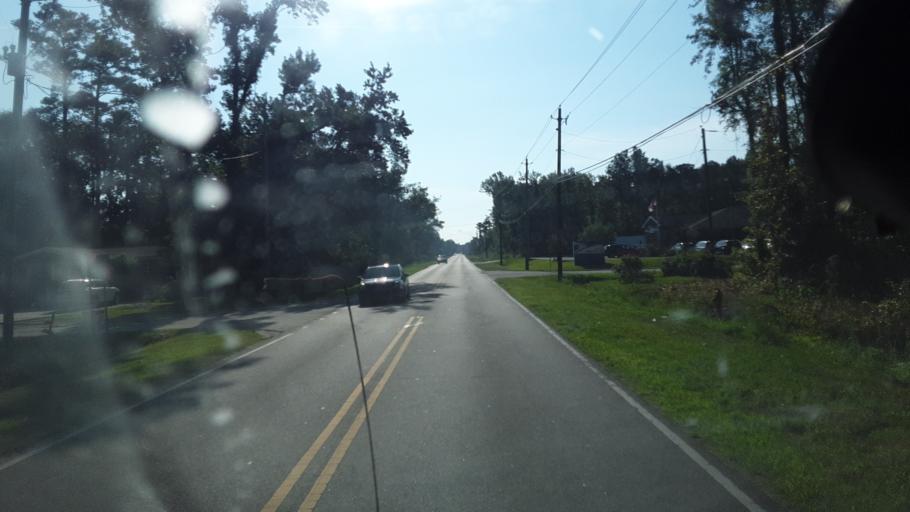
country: US
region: North Carolina
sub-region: Brunswick County
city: Leland
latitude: 34.2498
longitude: -78.0333
